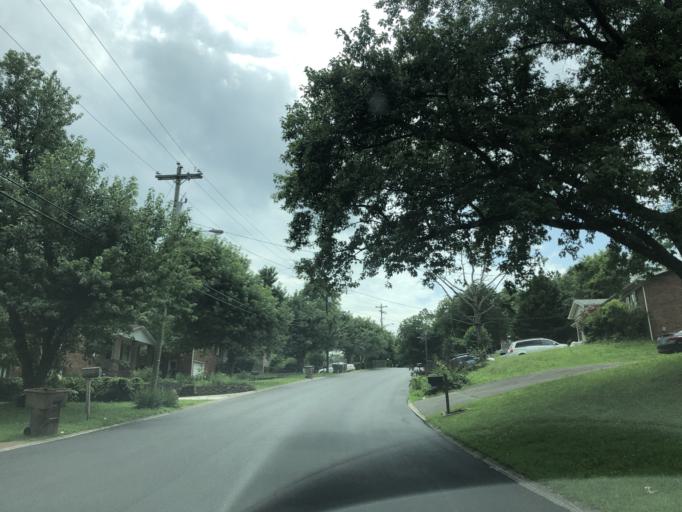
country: US
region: Tennessee
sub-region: Williamson County
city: Brentwood Estates
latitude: 36.0543
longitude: -86.6816
